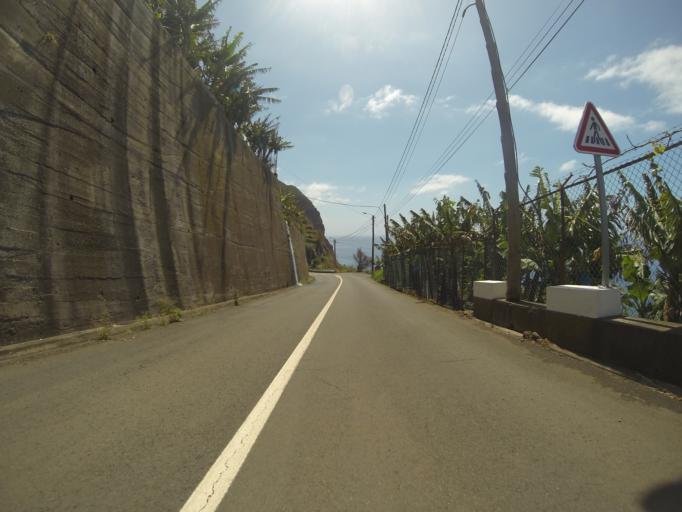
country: PT
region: Madeira
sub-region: Calheta
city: Arco da Calheta
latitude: 32.7077
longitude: -17.1460
